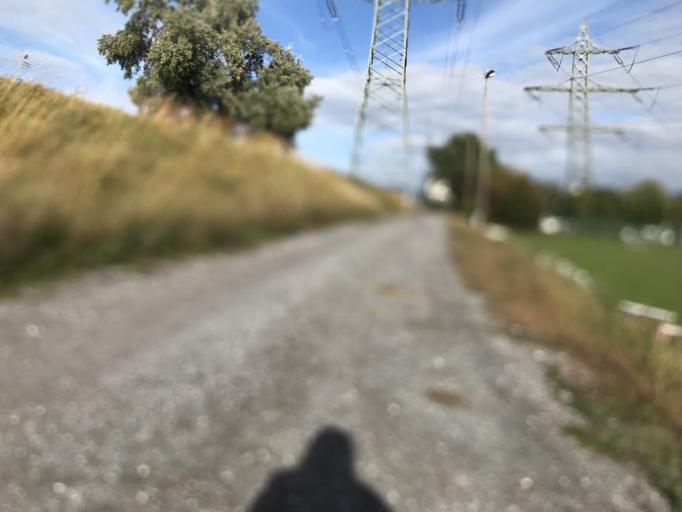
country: AT
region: Vorarlberg
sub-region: Politischer Bezirk Feldkirch
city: Mader
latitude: 47.3549
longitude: 9.6120
